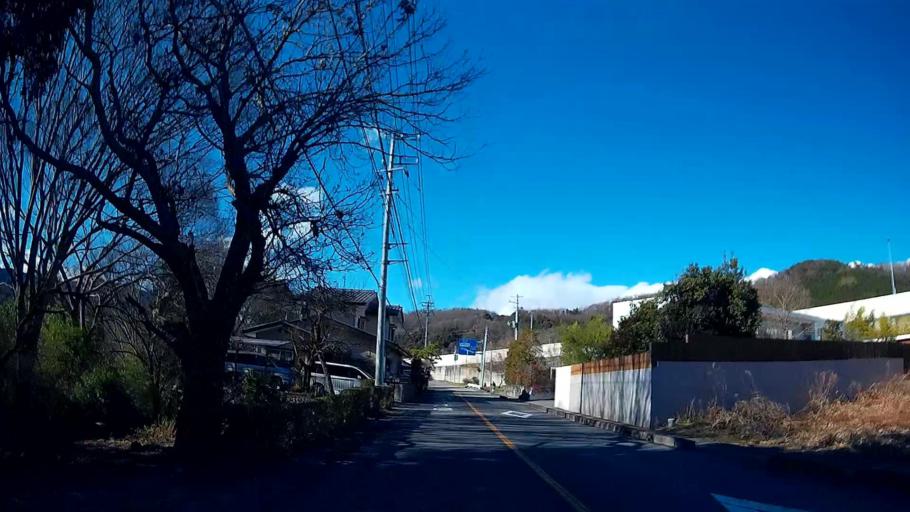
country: JP
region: Saitama
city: Yorii
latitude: 36.1193
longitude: 139.1815
